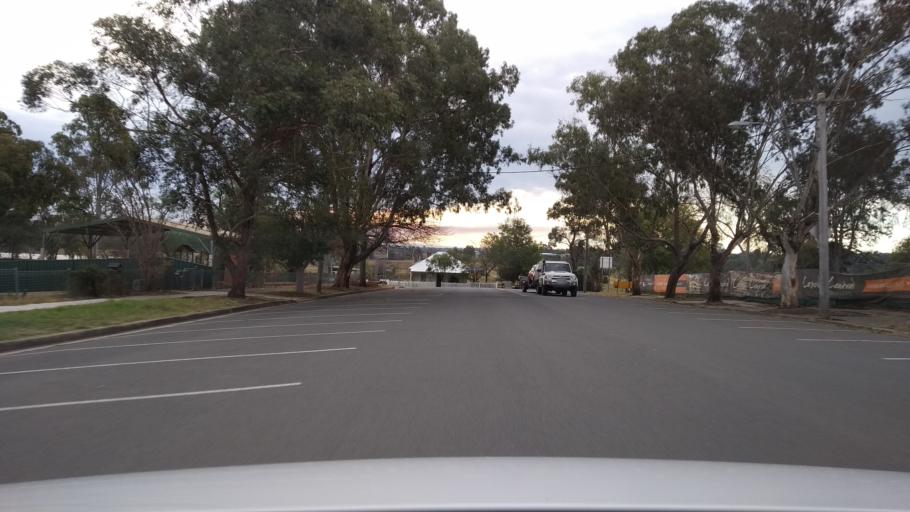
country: AU
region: New South Wales
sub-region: Camden
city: Elderslie
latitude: -34.0516
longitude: 150.6940
